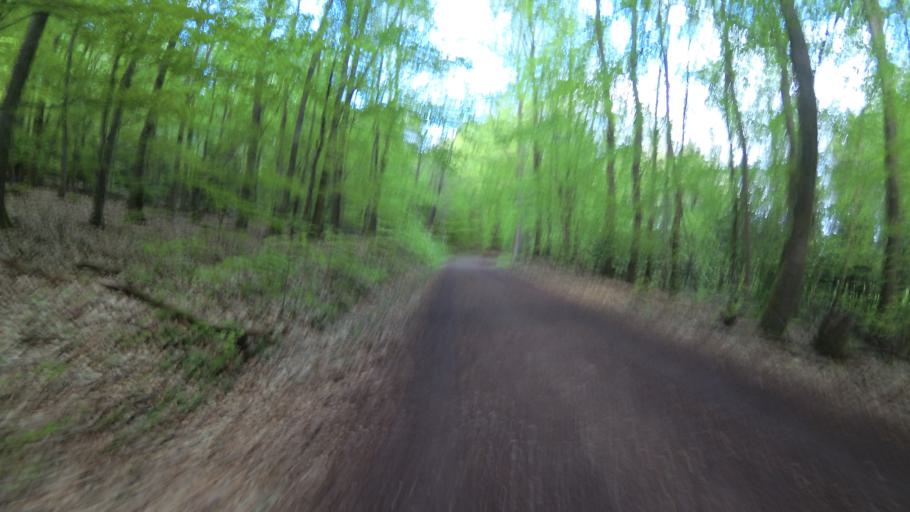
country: DE
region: Saarland
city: Marpingen
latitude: 49.4323
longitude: 7.0612
